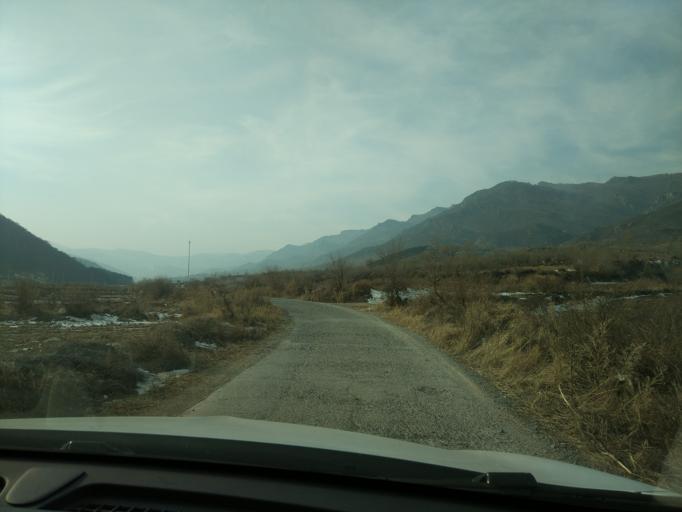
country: CN
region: Hebei
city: Xiwanzi
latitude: 40.8255
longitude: 115.5058
